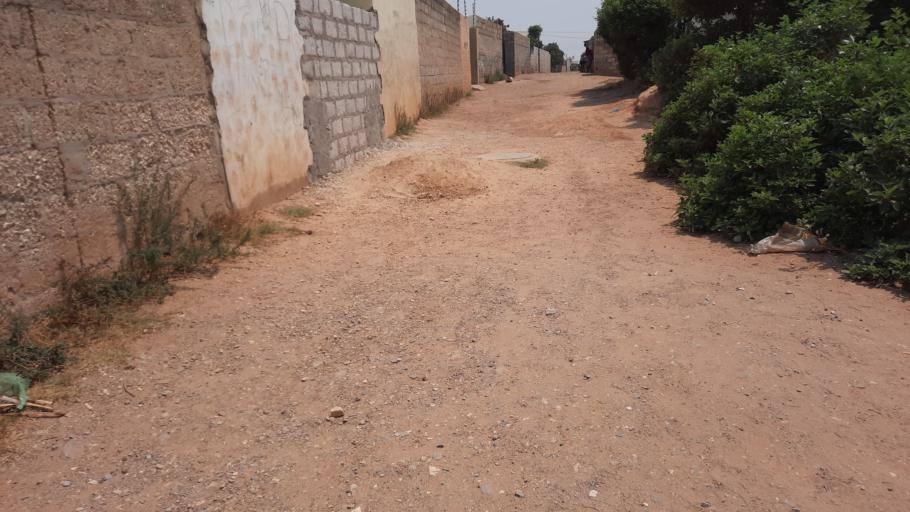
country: ZM
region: Lusaka
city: Lusaka
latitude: -15.3977
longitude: 28.3776
